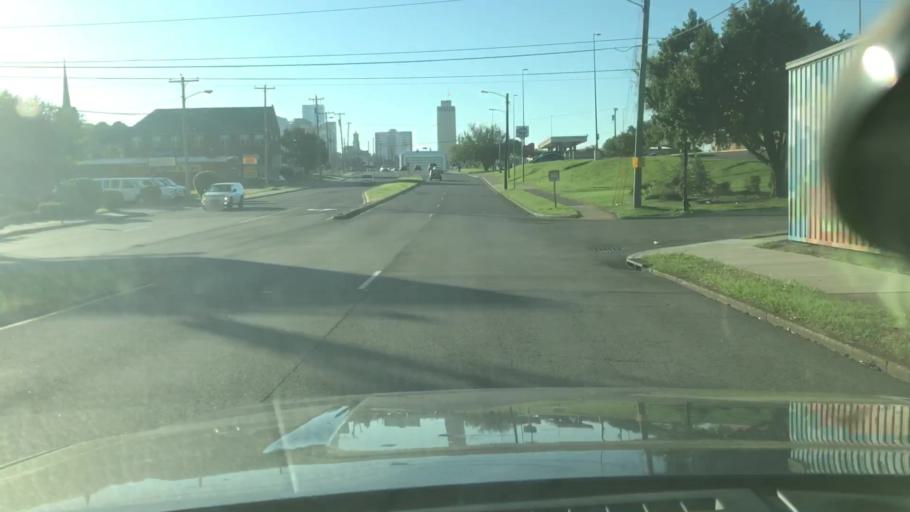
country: US
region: Tennessee
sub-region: Davidson County
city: Nashville
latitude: 36.1771
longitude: -86.7940
